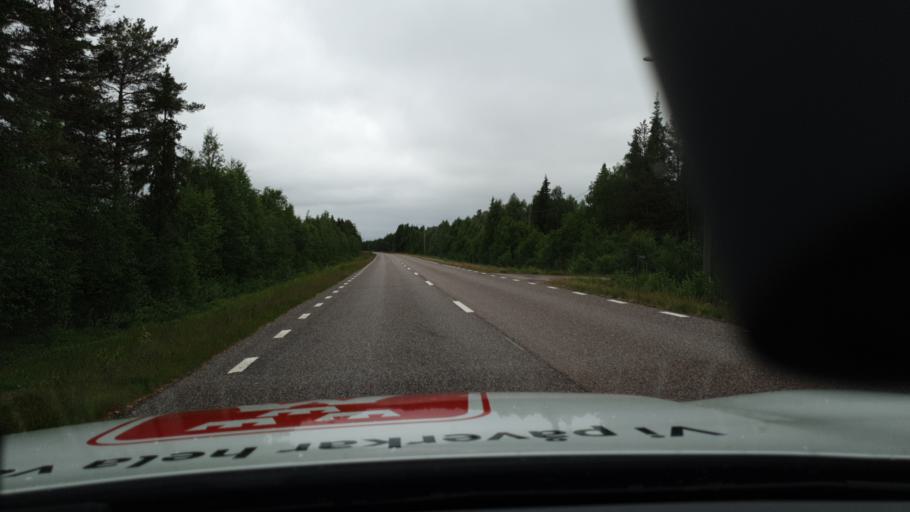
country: FI
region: Lapland
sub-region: Torniolaakso
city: Pello
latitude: 67.0032
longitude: 23.7541
